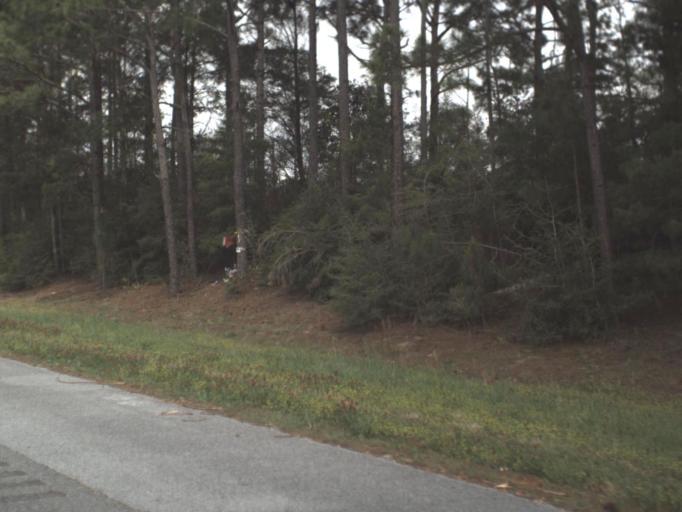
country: US
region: Florida
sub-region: Okaloosa County
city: Crestview
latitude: 30.7187
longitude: -86.4569
